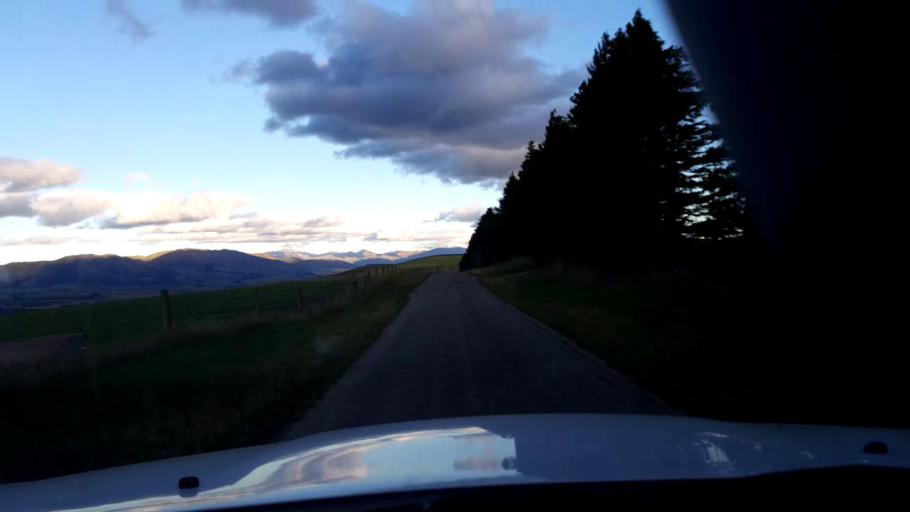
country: NZ
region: Canterbury
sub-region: Timaru District
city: Pleasant Point
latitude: -44.2583
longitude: 170.9150
